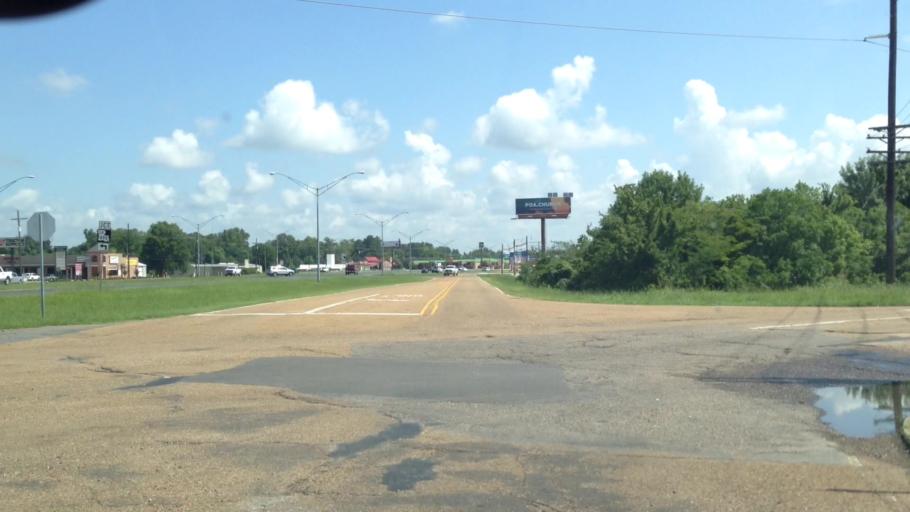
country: US
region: Louisiana
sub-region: Rapides Parish
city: Alexandria
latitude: 31.3051
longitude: -92.4794
